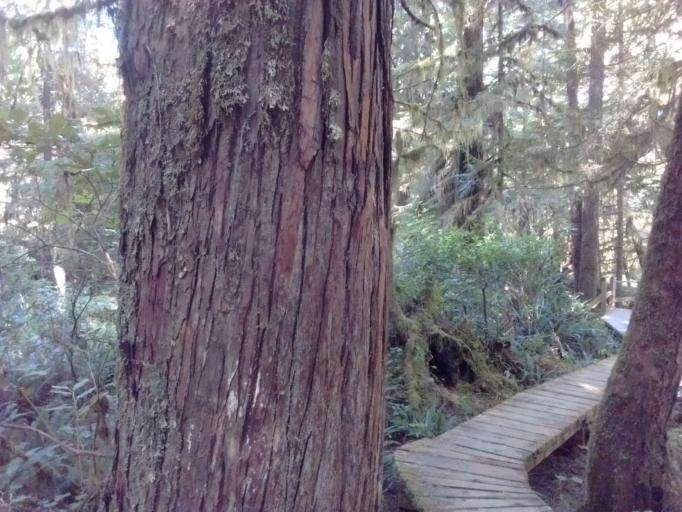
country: CA
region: British Columbia
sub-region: Regional District of Alberni-Clayoquot
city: Ucluelet
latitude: 49.0435
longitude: -125.6831
